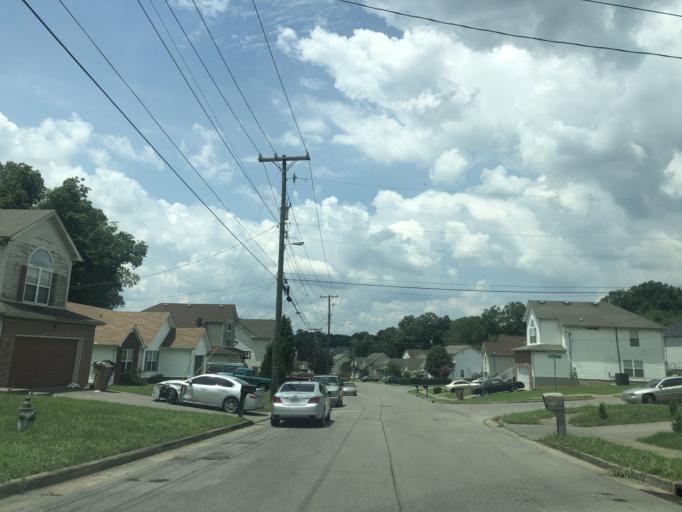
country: US
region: Tennessee
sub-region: Rutherford County
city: La Vergne
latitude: 36.0594
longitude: -86.6526
